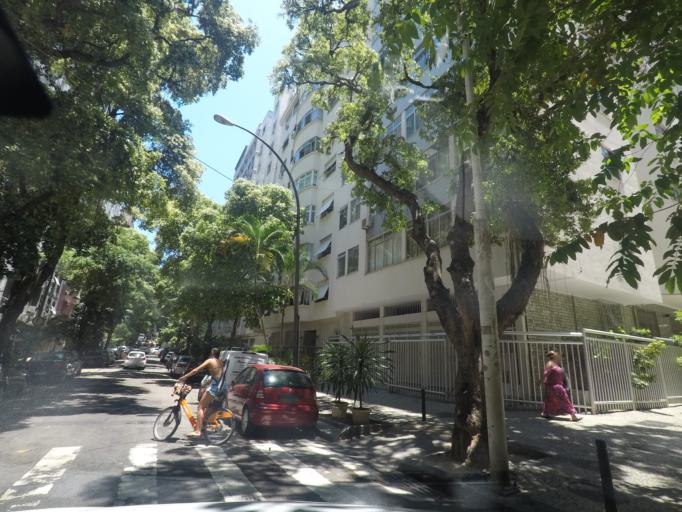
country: BR
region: Rio de Janeiro
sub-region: Rio De Janeiro
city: Rio de Janeiro
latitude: -22.9821
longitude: -43.1951
